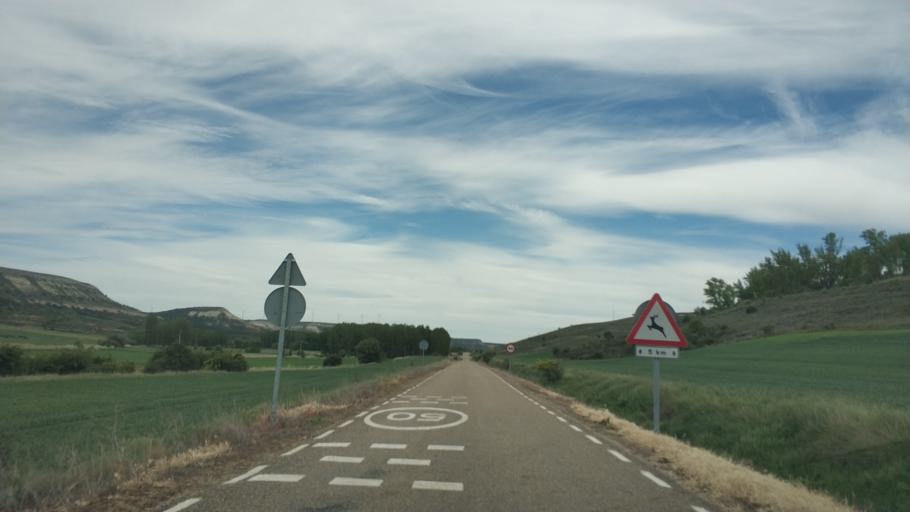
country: ES
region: Castille and Leon
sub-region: Provincia de Soria
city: Caltojar
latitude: 41.4298
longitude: -2.7947
